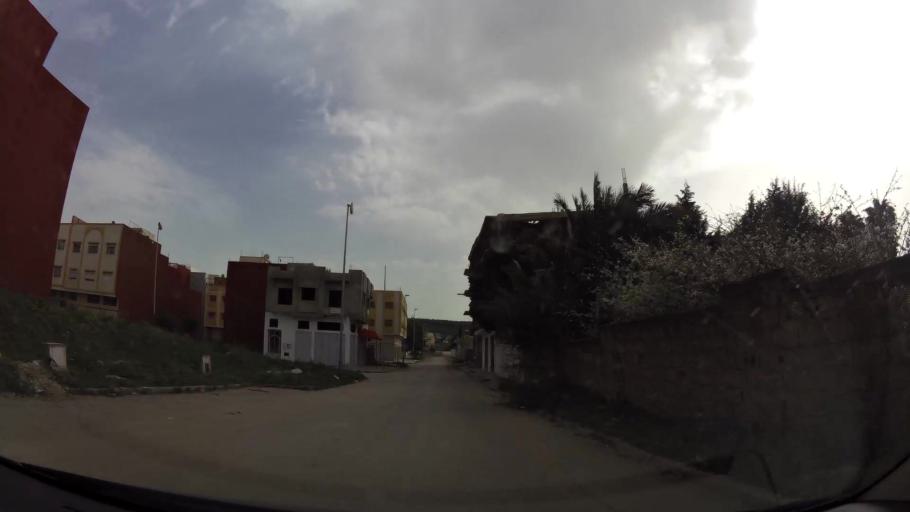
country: MA
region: Tanger-Tetouan
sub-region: Tanger-Assilah
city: Boukhalef
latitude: 35.7091
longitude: -5.8997
